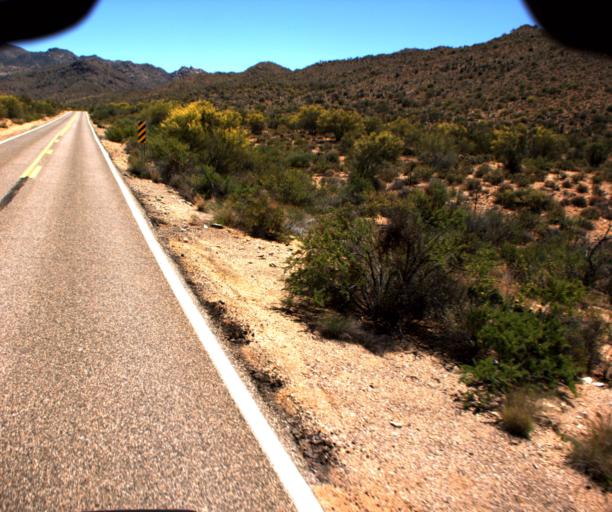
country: US
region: Arizona
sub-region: Yavapai County
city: Bagdad
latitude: 34.4657
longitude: -113.0457
